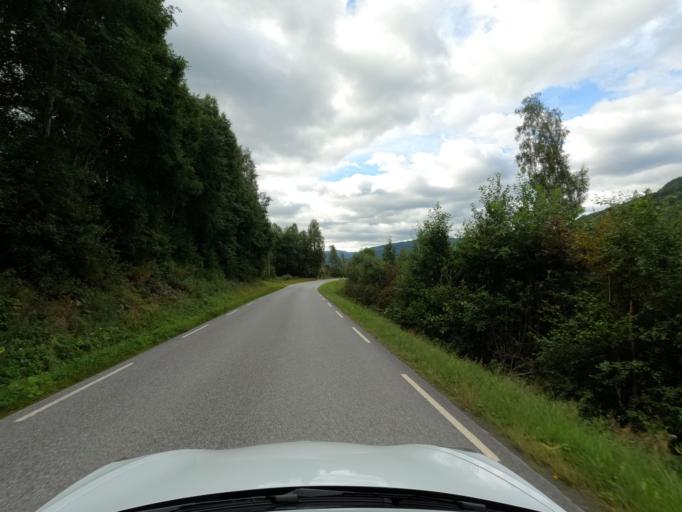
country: NO
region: Telemark
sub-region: Tinn
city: Rjukan
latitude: 60.0118
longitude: 8.8371
